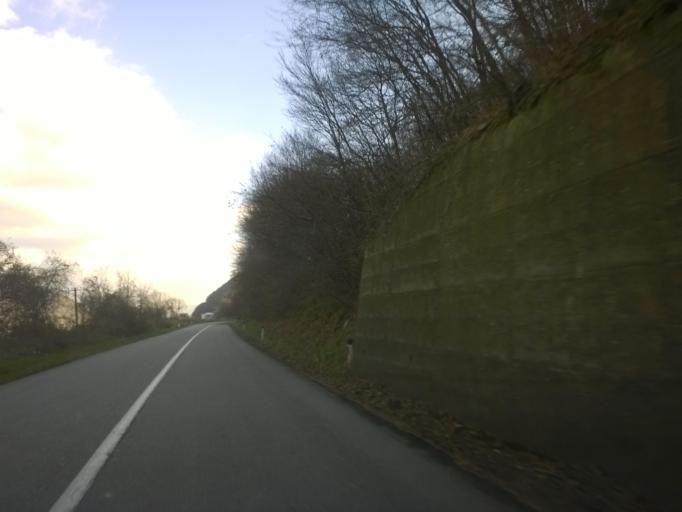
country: RS
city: Radenka
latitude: 44.6573
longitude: 21.7756
